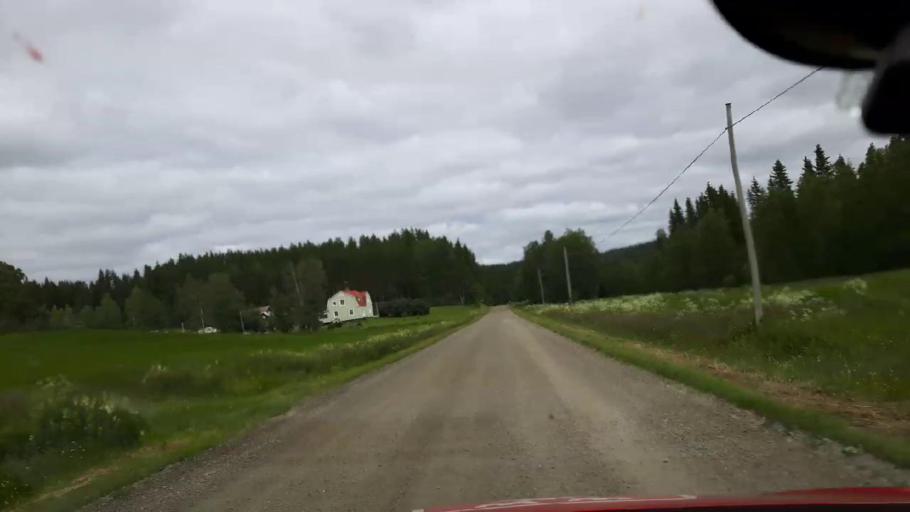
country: SE
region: Jaemtland
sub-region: OEstersunds Kommun
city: Brunflo
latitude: 62.9584
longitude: 15.0041
